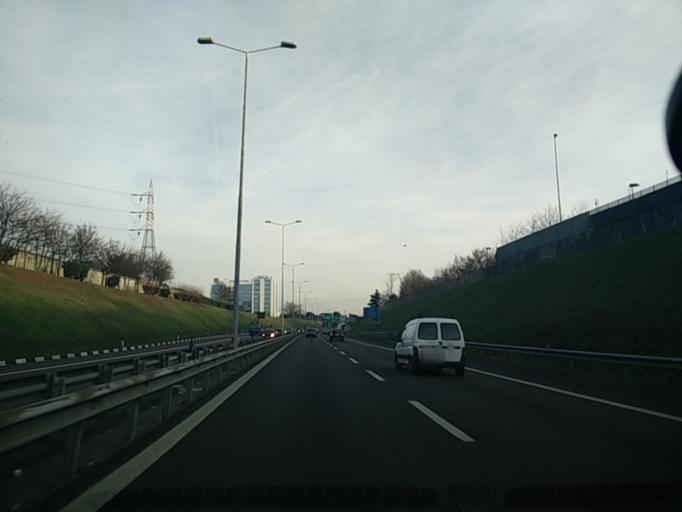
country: IT
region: Lombardy
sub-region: Citta metropolitana di Milano
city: Cinisello Balsamo
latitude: 45.5648
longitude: 9.2333
